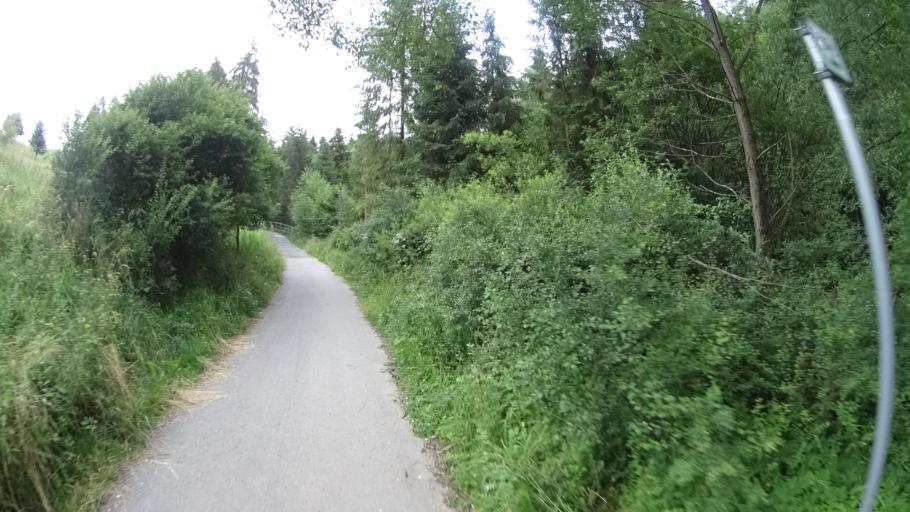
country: PL
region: Lesser Poland Voivodeship
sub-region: Powiat nowotarski
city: Kluszkowce
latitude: 49.4371
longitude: 20.3139
